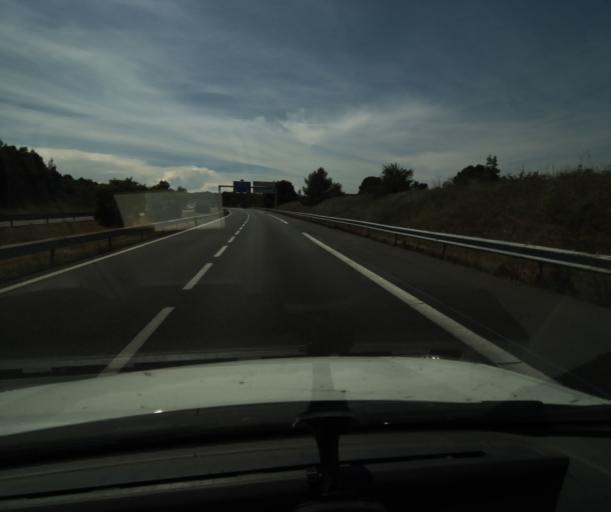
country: FR
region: Languedoc-Roussillon
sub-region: Departement de l'Aude
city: Trebes
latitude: 43.1964
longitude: 2.4248
